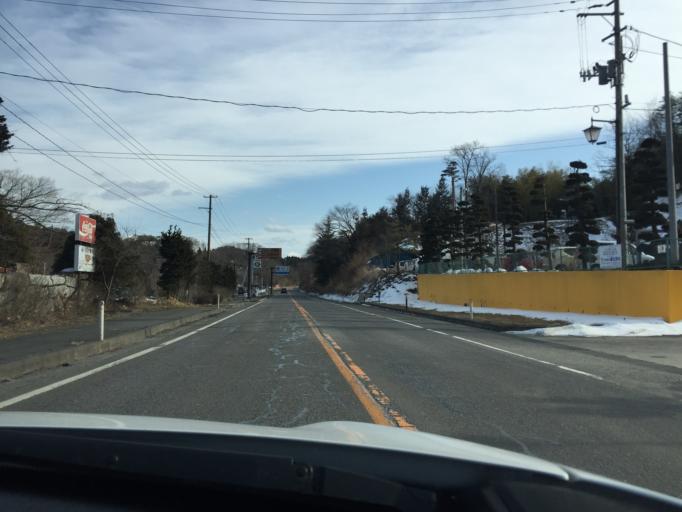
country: JP
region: Fukushima
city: Ishikawa
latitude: 37.2707
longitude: 140.5506
